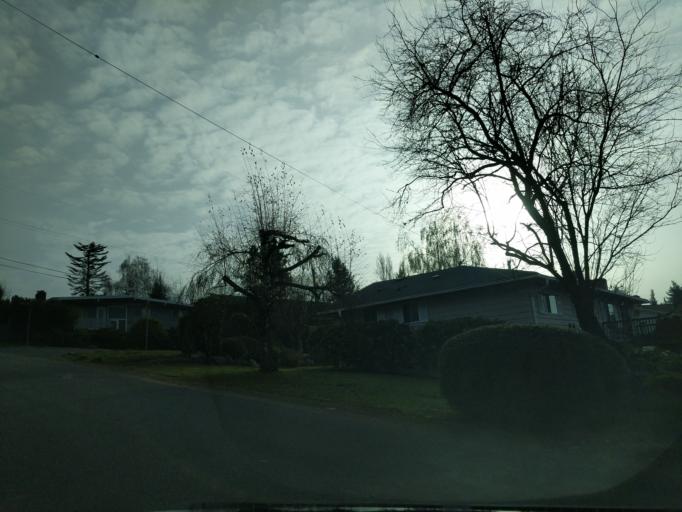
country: US
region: Washington
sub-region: King County
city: Shoreline
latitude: 47.7487
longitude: -122.3264
